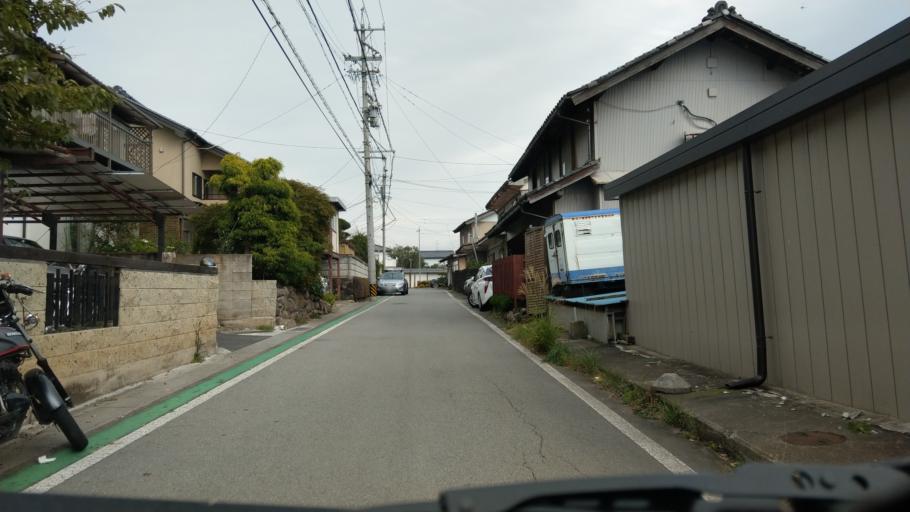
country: JP
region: Nagano
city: Komoro
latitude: 36.3397
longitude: 138.3957
